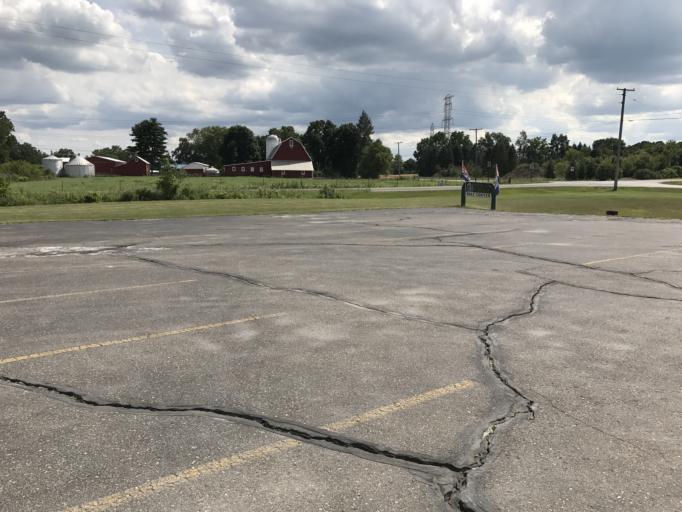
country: US
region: Michigan
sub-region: Washtenaw County
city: Ann Arbor
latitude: 42.3549
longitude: -83.6819
